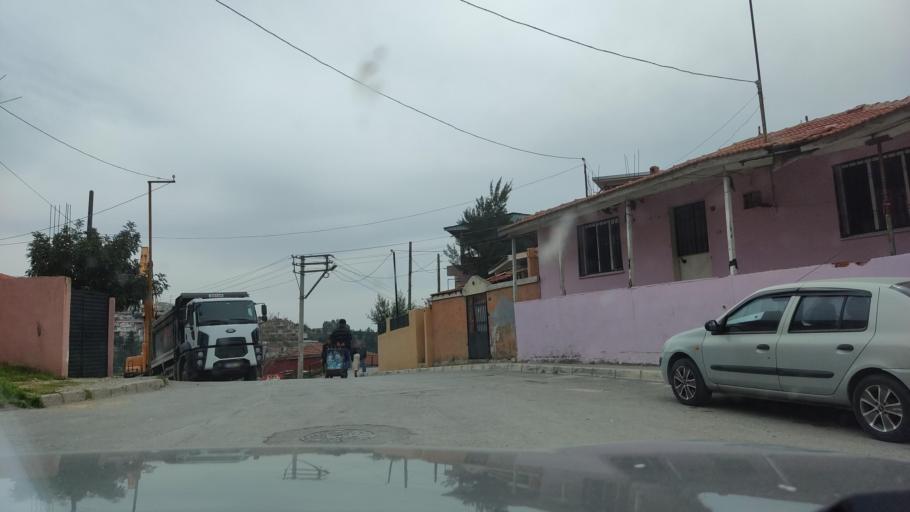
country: TR
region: Izmir
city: Karsiyaka
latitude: 38.5021
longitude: 27.0780
